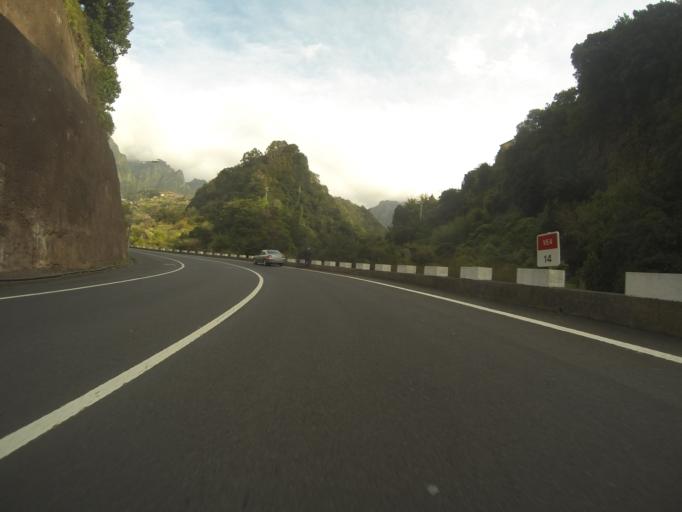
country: PT
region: Madeira
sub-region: Sao Vicente
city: Sao Vicente
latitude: 32.7905
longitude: -17.0339
